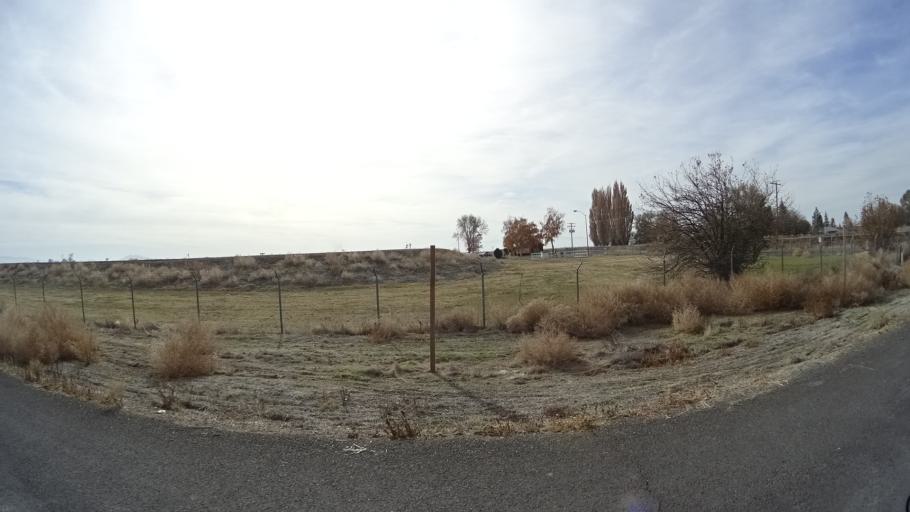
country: US
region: California
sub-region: Siskiyou County
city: Tulelake
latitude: 41.9492
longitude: -121.4710
